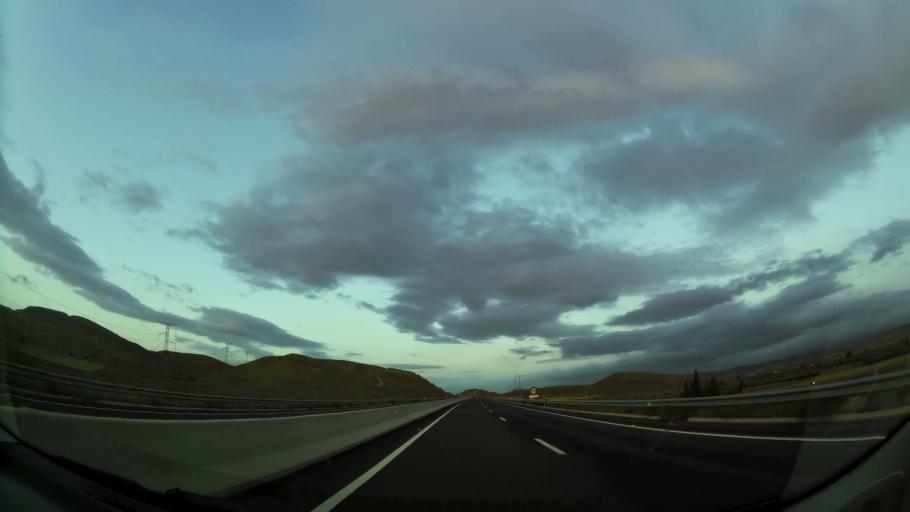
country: MA
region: Oriental
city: El Aioun
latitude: 34.5948
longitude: -2.6738
